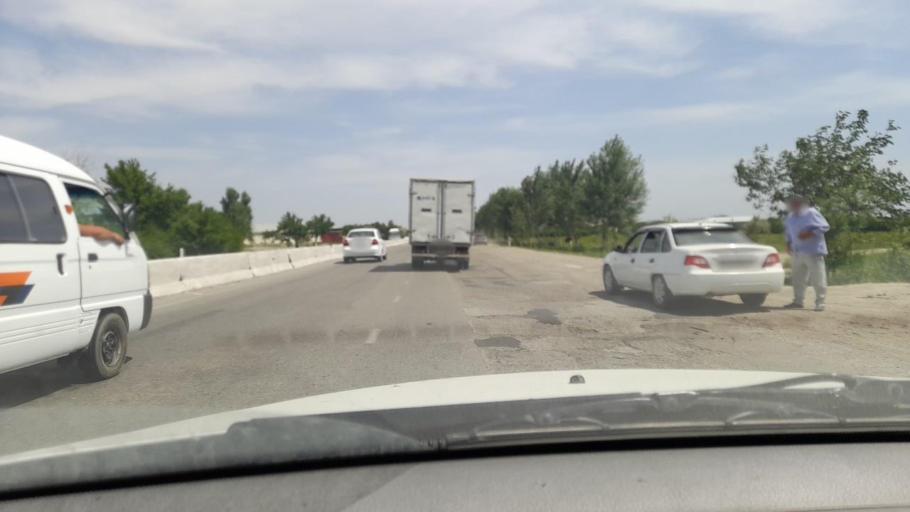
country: UZ
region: Bukhara
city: Wobkent
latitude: 40.0566
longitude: 64.5434
